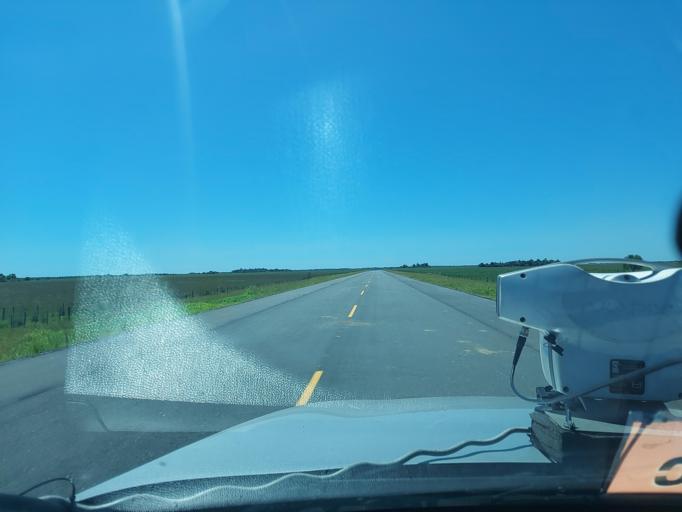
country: PY
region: Neembucu
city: Pilar
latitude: -26.8260
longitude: -58.2425
